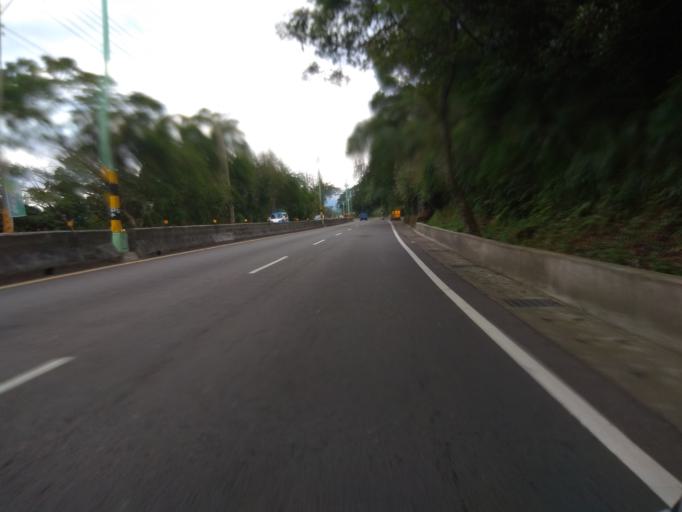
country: TW
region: Taiwan
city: Daxi
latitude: 24.8488
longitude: 121.2069
